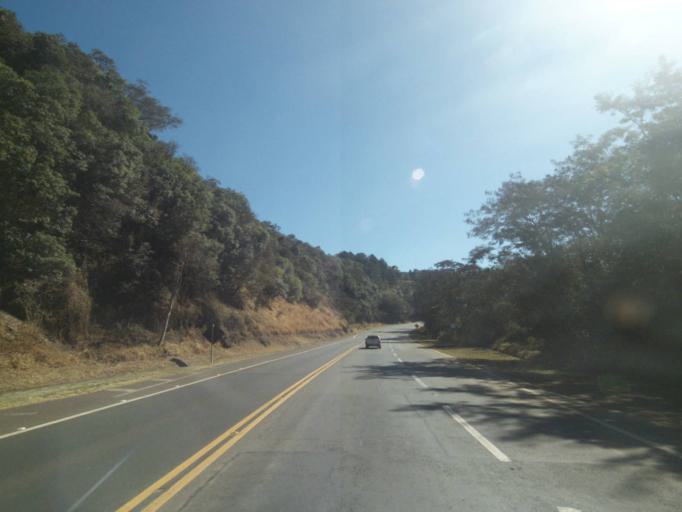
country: BR
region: Parana
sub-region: Tibagi
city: Tibagi
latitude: -24.7101
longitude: -50.5551
